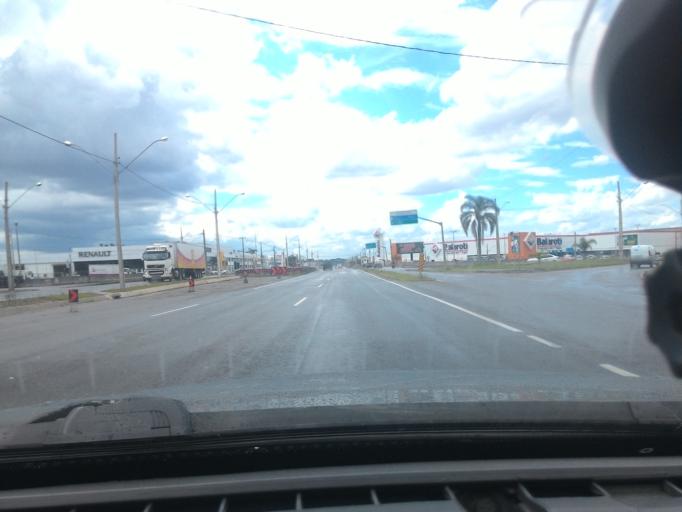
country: BR
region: Parana
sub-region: Sao Jose Dos Pinhais
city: Sao Jose dos Pinhais
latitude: -25.5314
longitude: -49.1953
